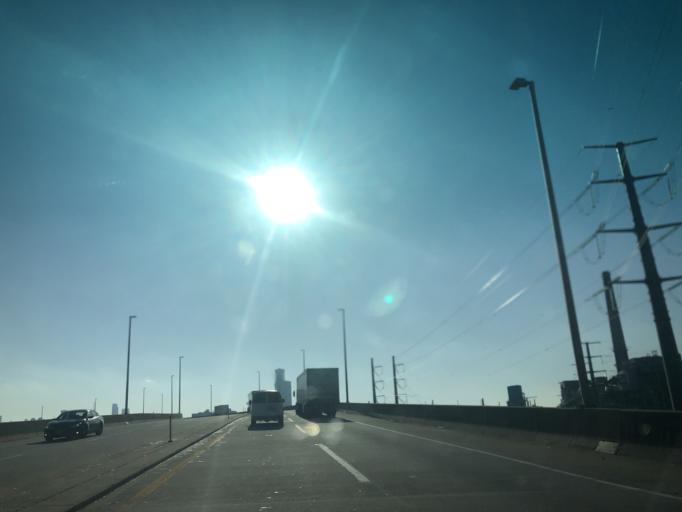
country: US
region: New Jersey
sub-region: Hudson County
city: Jersey City
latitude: 40.7527
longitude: -74.0715
